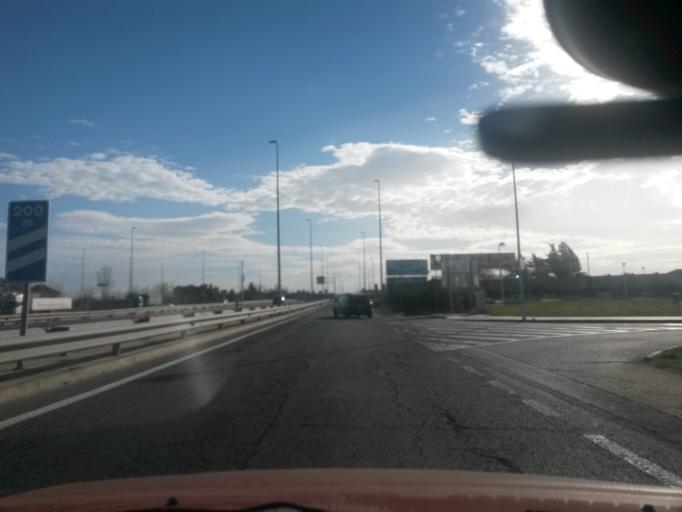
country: ES
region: Castille and Leon
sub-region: Provincia de Salamanca
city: Carbajosa de la Sagrada
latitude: 40.9486
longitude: -5.6492
